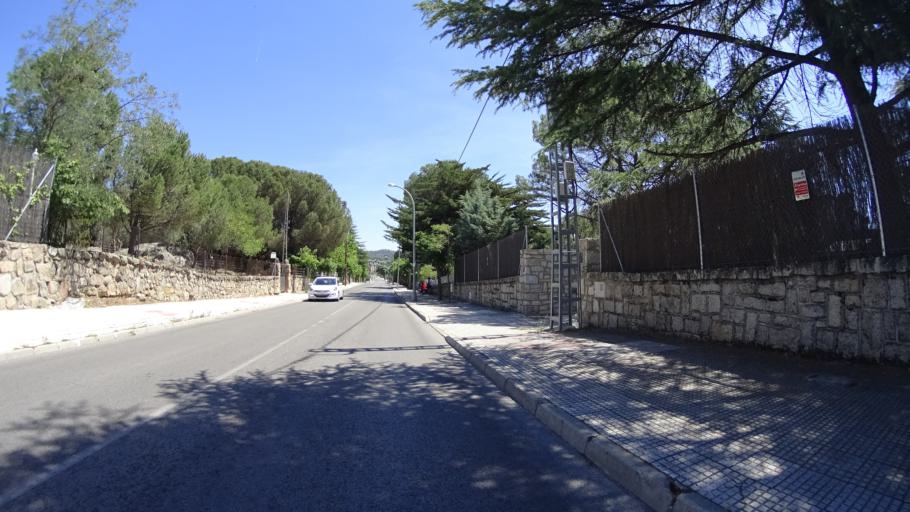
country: ES
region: Madrid
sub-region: Provincia de Madrid
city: Hoyo de Manzanares
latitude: 40.6179
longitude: -3.9173
